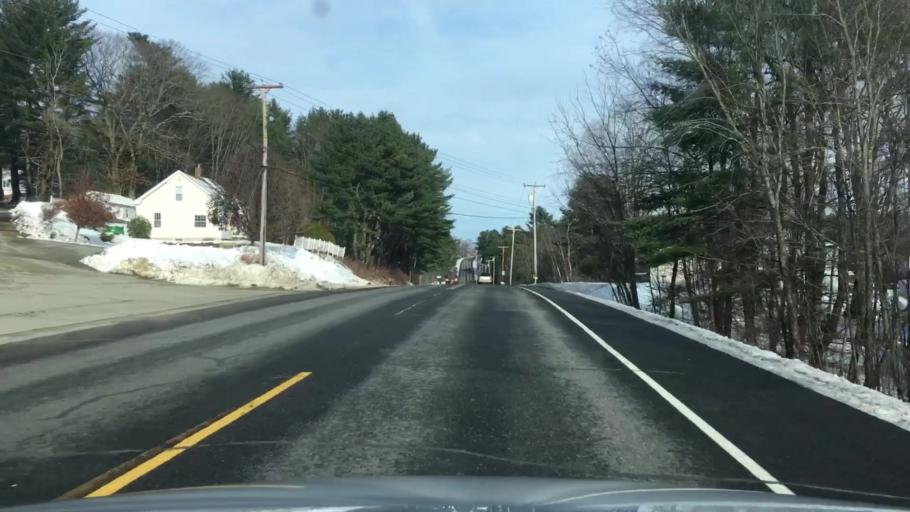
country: US
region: Maine
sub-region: Androscoggin County
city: Greene
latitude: 44.1668
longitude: -70.1787
